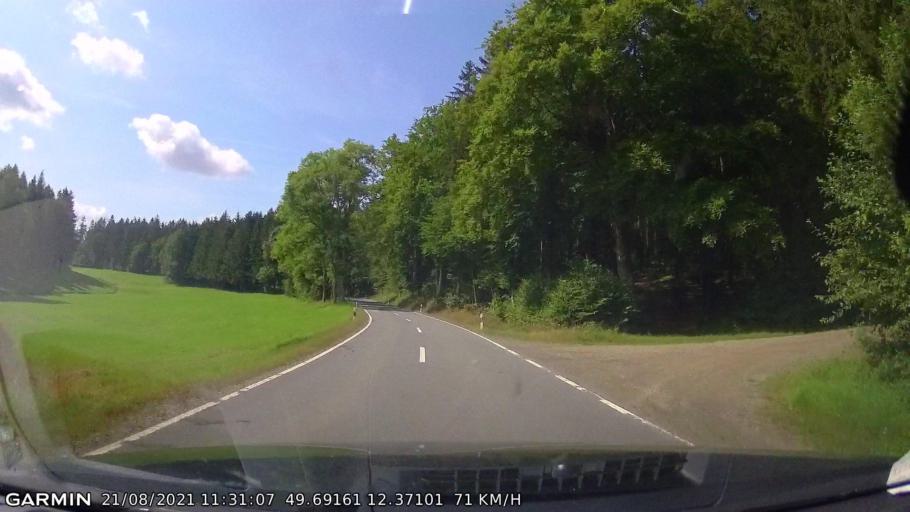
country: DE
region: Bavaria
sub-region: Upper Palatinate
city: Waldthurn
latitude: 49.6915
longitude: 12.3709
